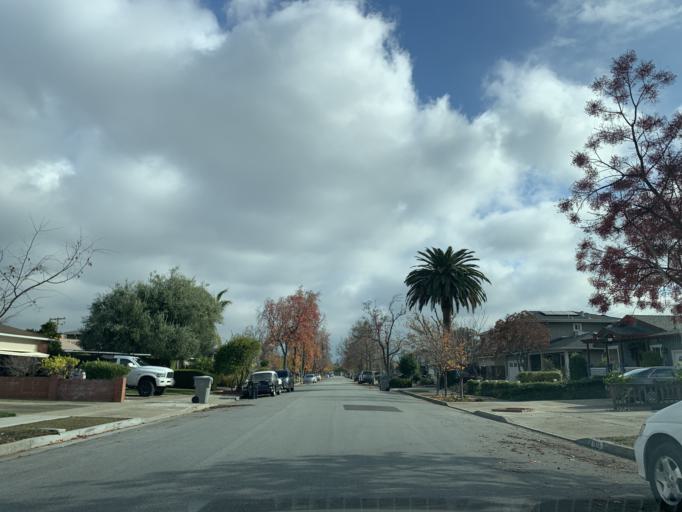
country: US
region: California
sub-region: Santa Clara County
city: Cambrian Park
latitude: 37.2548
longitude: -121.9207
